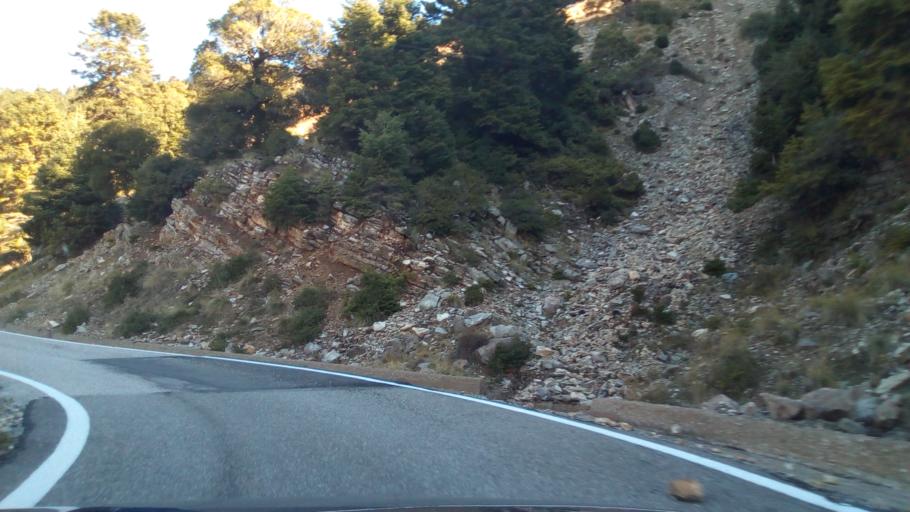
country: GR
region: West Greece
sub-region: Nomos Aitolias kai Akarnanias
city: Nafpaktos
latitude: 38.5271
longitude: 21.8478
